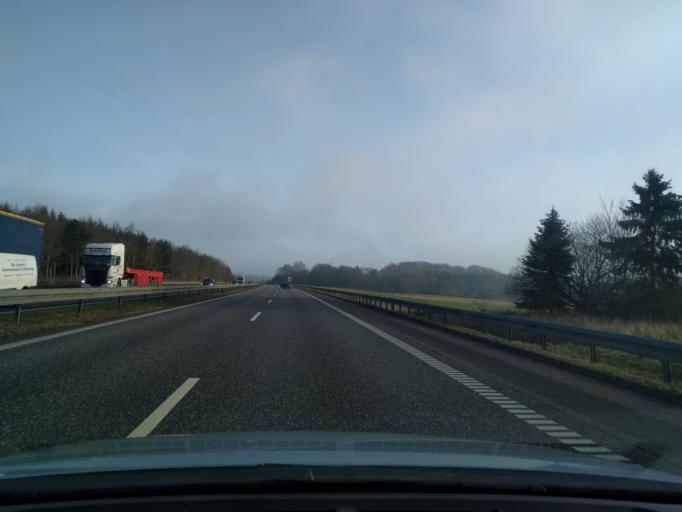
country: DK
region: Zealand
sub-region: Soro Kommune
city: Soro
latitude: 55.4407
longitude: 11.5073
